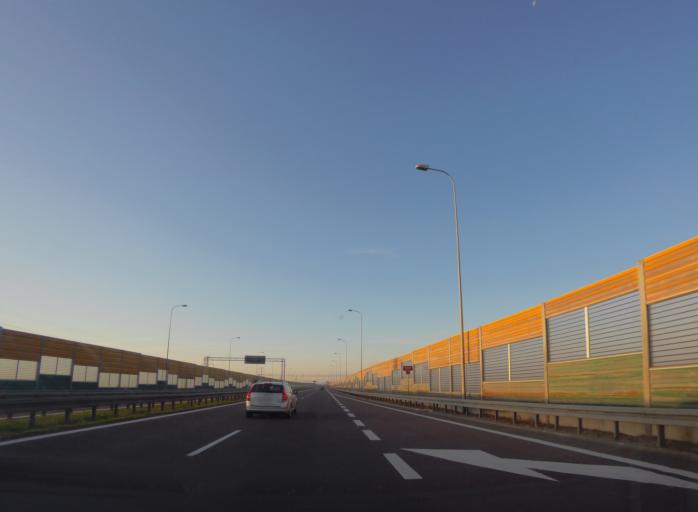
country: PL
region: Subcarpathian Voivodeship
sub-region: Powiat rzeszowski
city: Wolka Podlesna
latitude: 50.1145
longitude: 22.0745
